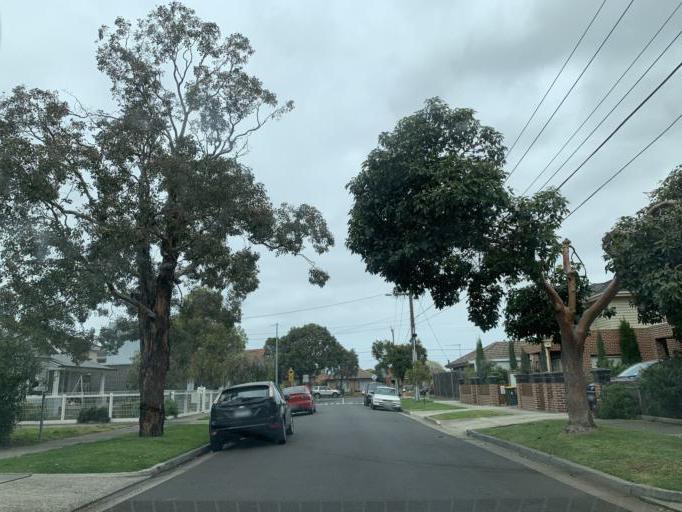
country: AU
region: Victoria
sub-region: Moreland
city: Pascoe Vale South
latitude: -37.7461
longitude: 144.9467
